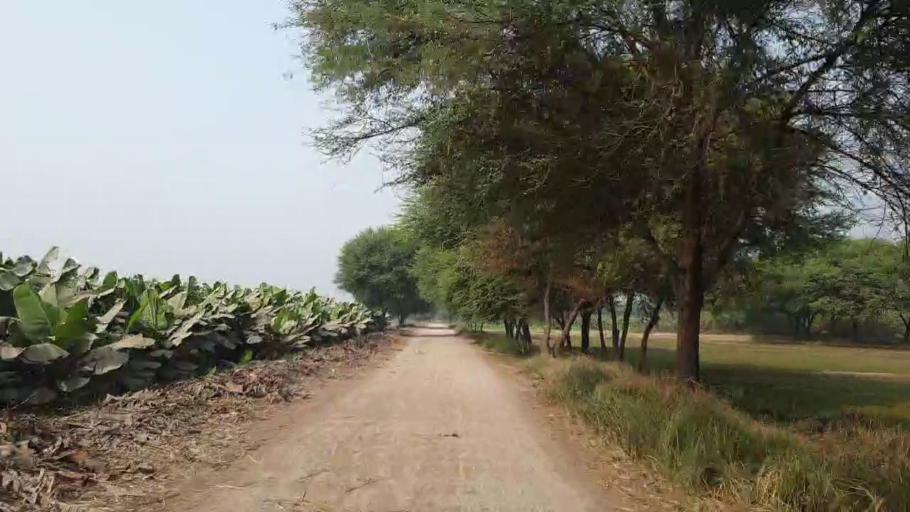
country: PK
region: Sindh
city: Tando Muhammad Khan
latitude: 25.2136
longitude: 68.5568
